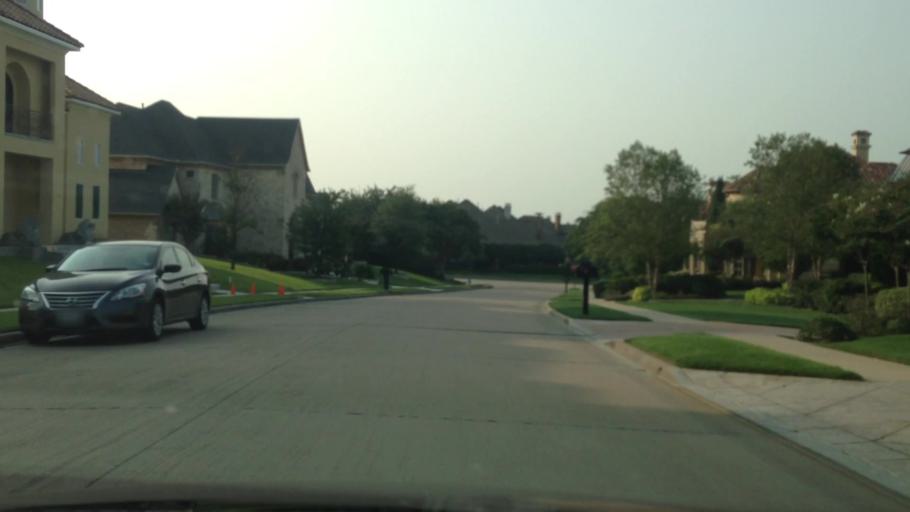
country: US
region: Texas
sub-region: Collin County
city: Frisco
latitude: 33.1252
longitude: -96.8377
